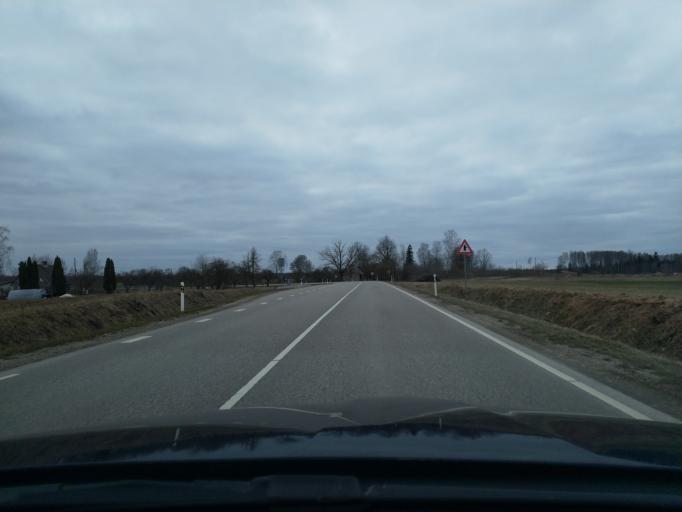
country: LV
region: Talsu Rajons
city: Sabile
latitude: 56.9308
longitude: 22.5353
